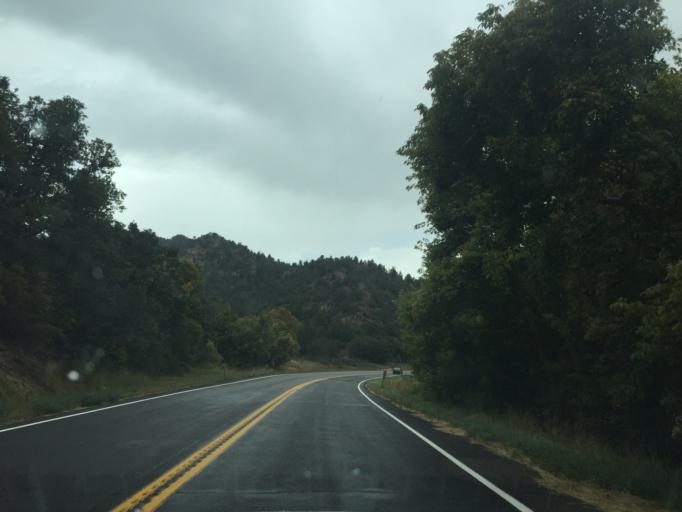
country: US
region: Utah
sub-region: Kane County
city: Kanab
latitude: 37.3549
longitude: -112.5985
